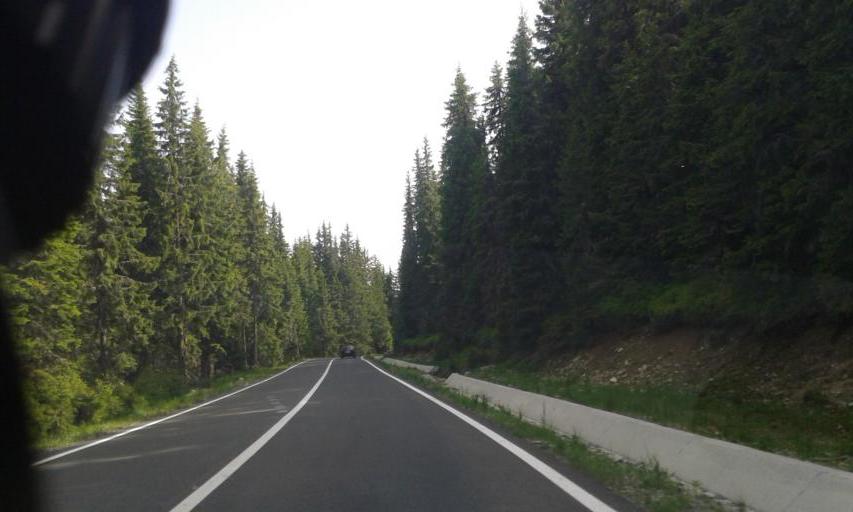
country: RO
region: Hunedoara
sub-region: Oras Petrila
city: Petrila
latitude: 45.4770
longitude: 23.6403
